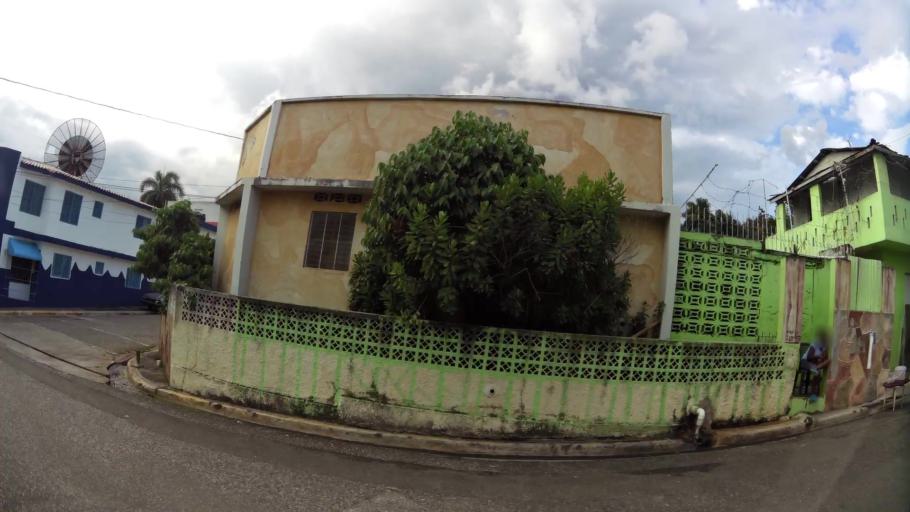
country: DO
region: San Cristobal
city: Villa Altagracia
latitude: 18.6720
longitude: -70.1719
